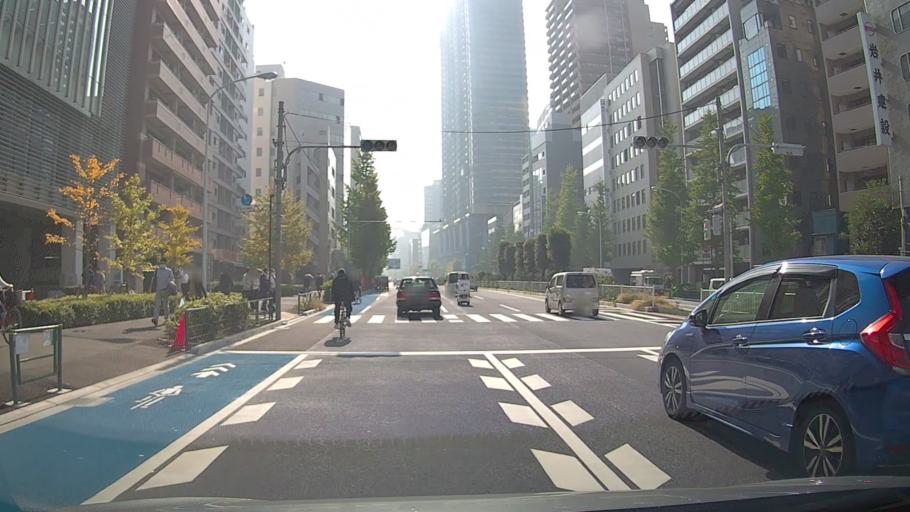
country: JP
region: Tokyo
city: Tokyo
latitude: 35.7131
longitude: 139.7525
